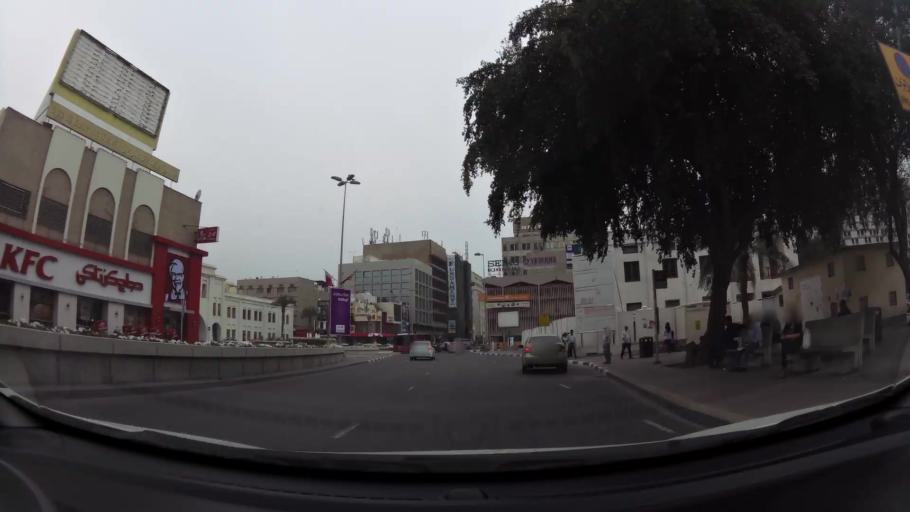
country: BH
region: Manama
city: Manama
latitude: 26.2348
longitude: 50.5757
